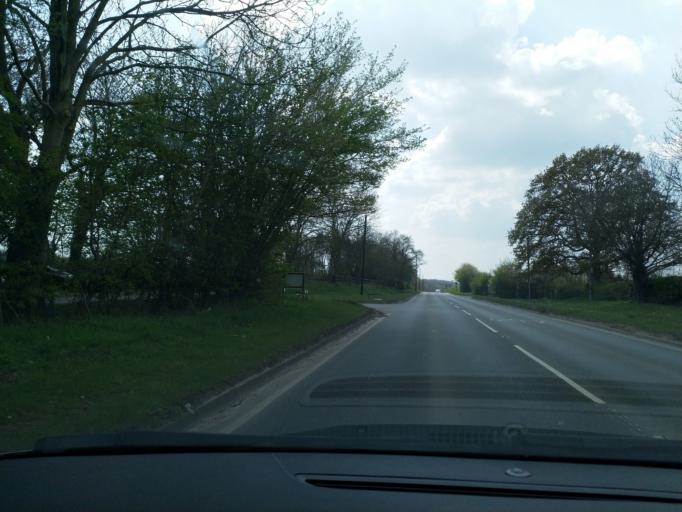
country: GB
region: England
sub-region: Warwickshire
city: Ryton on Dunsmore
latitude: 52.3470
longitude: -1.4688
